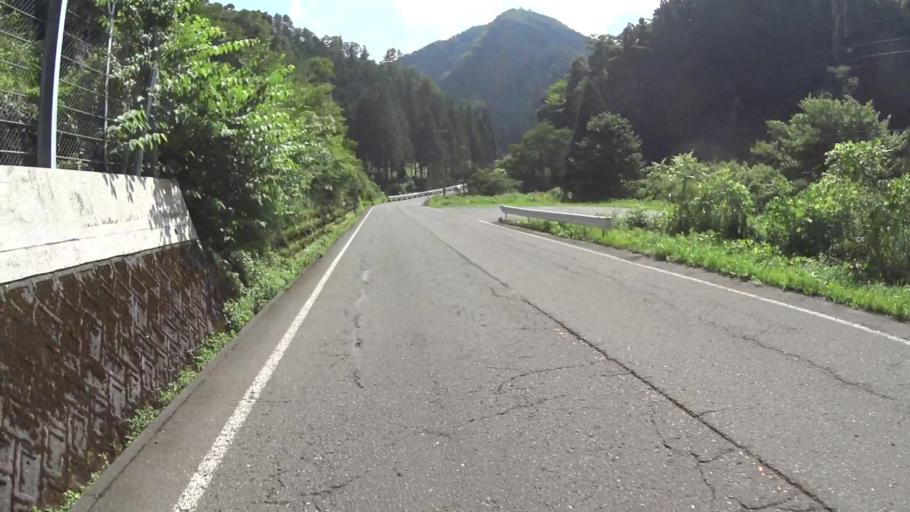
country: JP
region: Fukui
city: Obama
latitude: 35.3906
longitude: 135.5841
